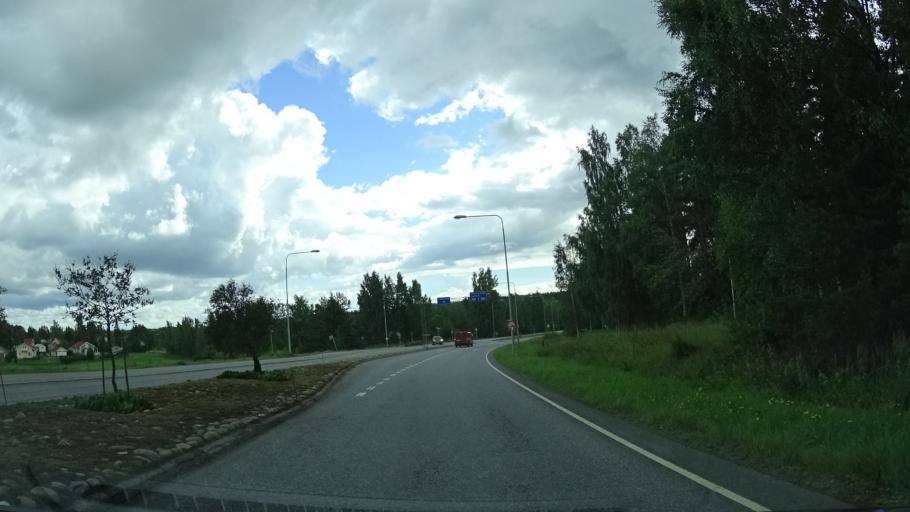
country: FI
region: Pirkanmaa
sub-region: Etelae-Pirkanmaa
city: Valkeakoski
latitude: 61.2536
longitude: 24.0338
